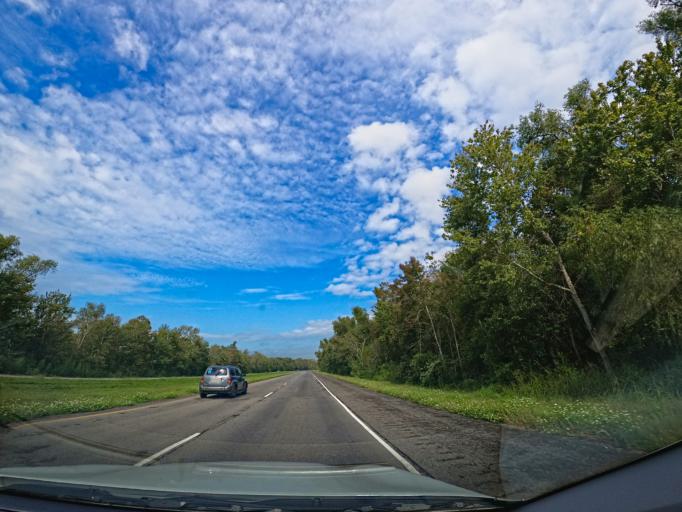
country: US
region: Louisiana
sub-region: Saint Mary Parish
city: Patterson
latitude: 29.7163
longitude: -91.4027
